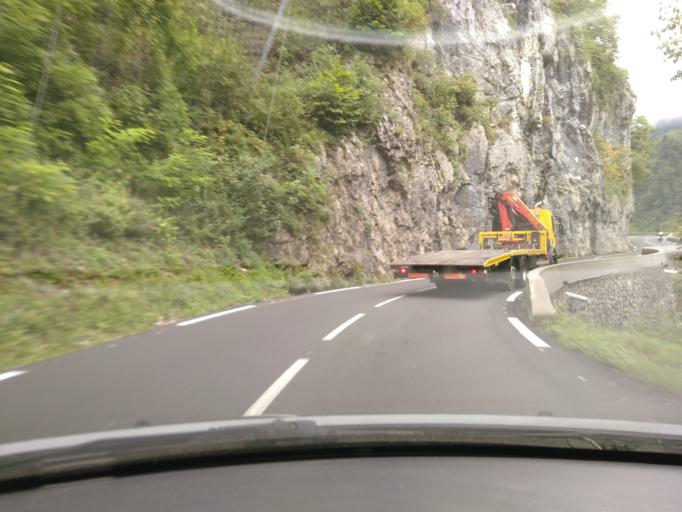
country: FR
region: Rhone-Alpes
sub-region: Departement de la Haute-Savoie
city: Bonneville
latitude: 46.0455
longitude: 6.3782
